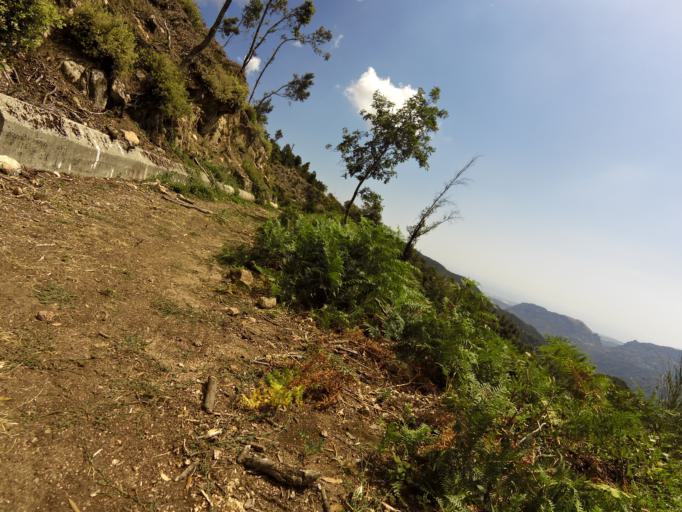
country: IT
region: Calabria
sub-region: Provincia di Vibo-Valentia
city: Nardodipace
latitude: 38.5080
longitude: 16.3936
